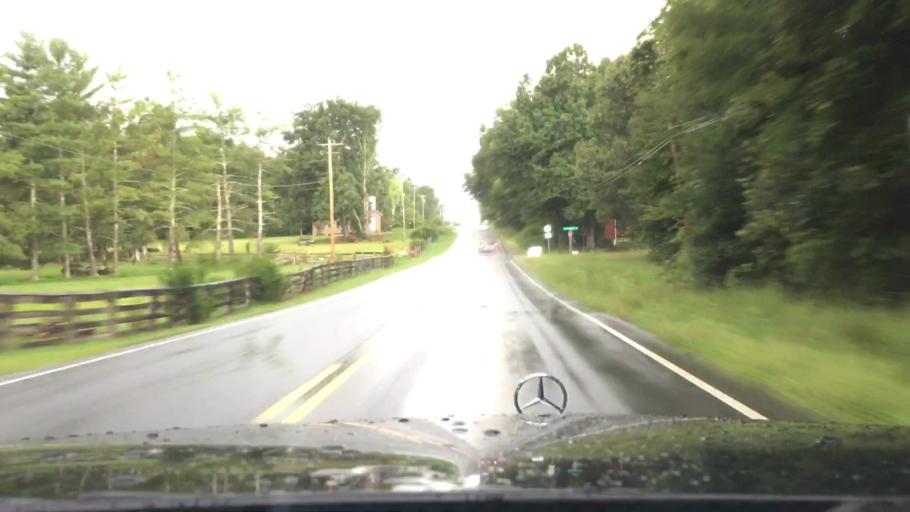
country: US
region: Virginia
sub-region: Nelson County
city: Lovingston
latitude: 37.7278
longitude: -79.0109
